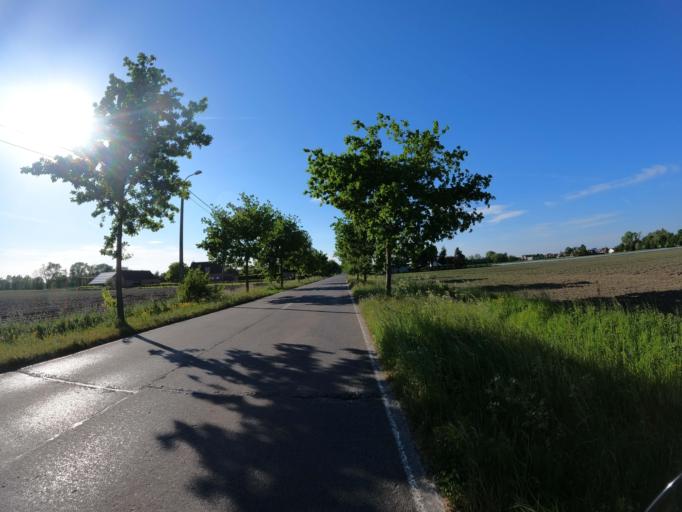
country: BE
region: Flanders
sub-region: Provincie Oost-Vlaanderen
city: Nazareth
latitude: 50.9734
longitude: 3.5732
